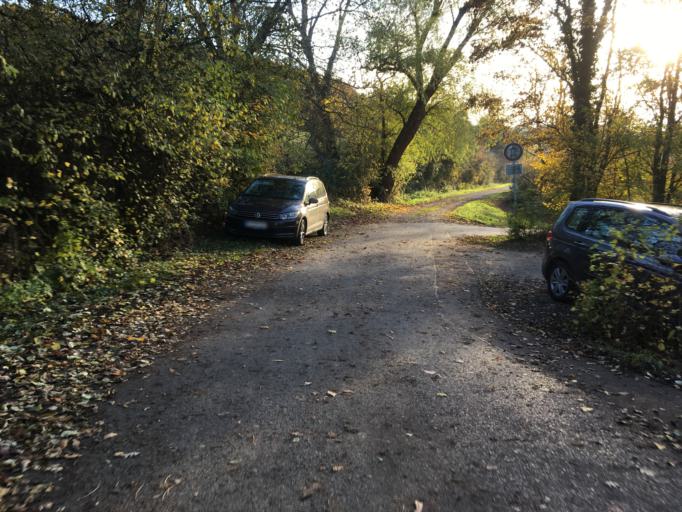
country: DE
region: Baden-Wuerttemberg
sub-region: Regierungsbezirk Stuttgart
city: Neckarwestheim
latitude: 49.0407
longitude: 9.2167
